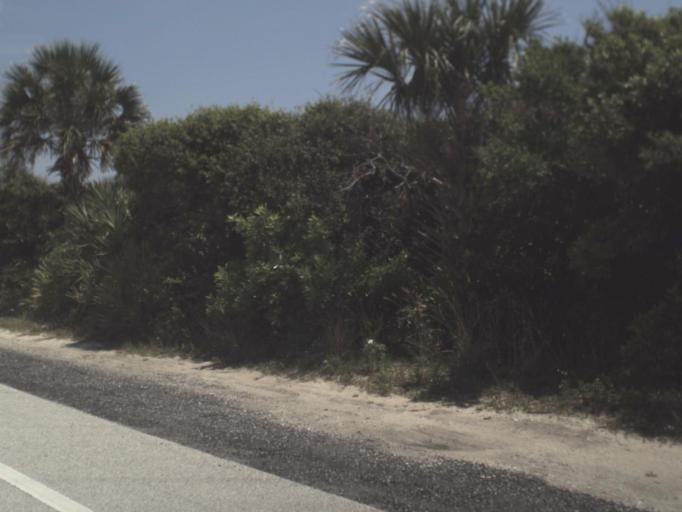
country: US
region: Florida
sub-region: Saint Johns County
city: Palm Valley
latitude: 30.1121
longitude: -81.3445
